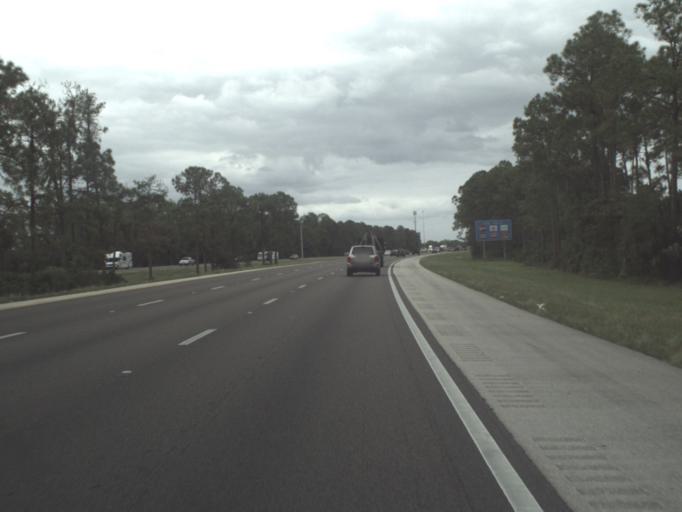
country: US
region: Florida
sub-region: Collier County
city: Vineyards
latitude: 26.2611
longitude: -81.7420
